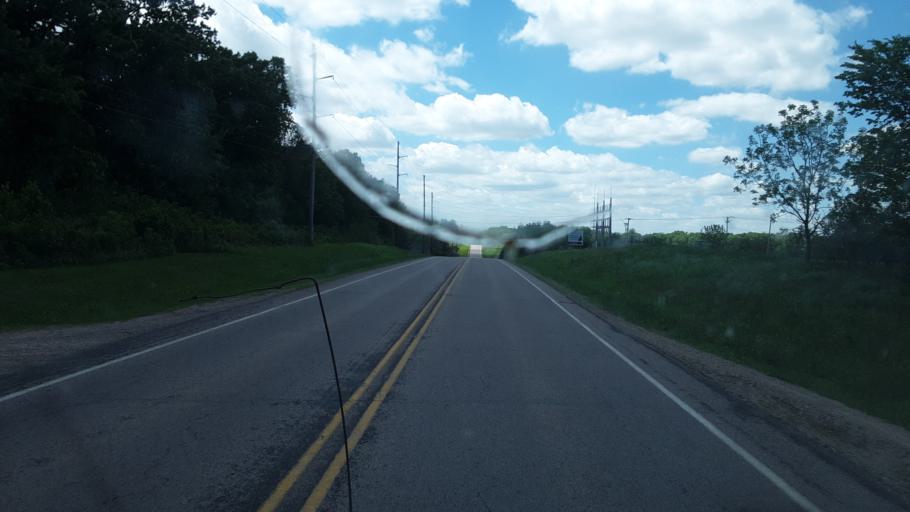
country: US
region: Wisconsin
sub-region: Sauk County
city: Lake Delton
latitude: 43.5910
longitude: -89.8652
